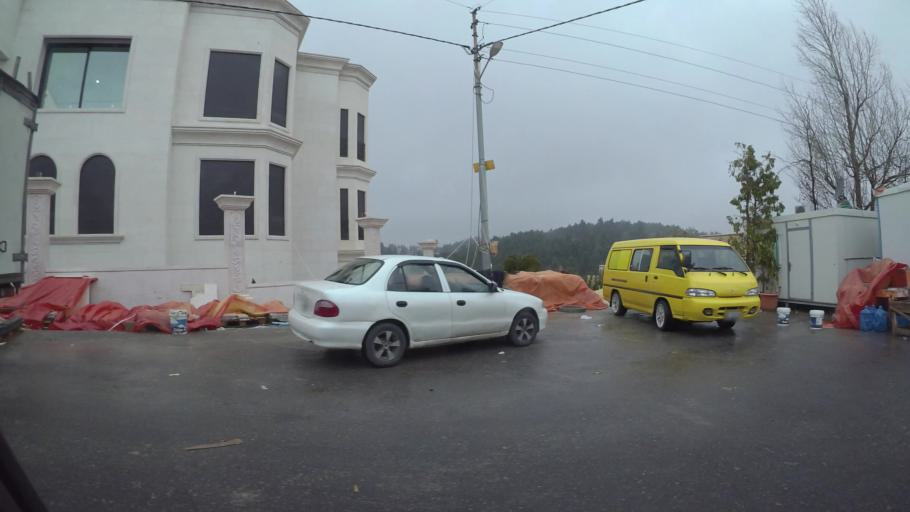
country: JO
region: Amman
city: Al Jubayhah
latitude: 32.0065
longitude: 35.8195
